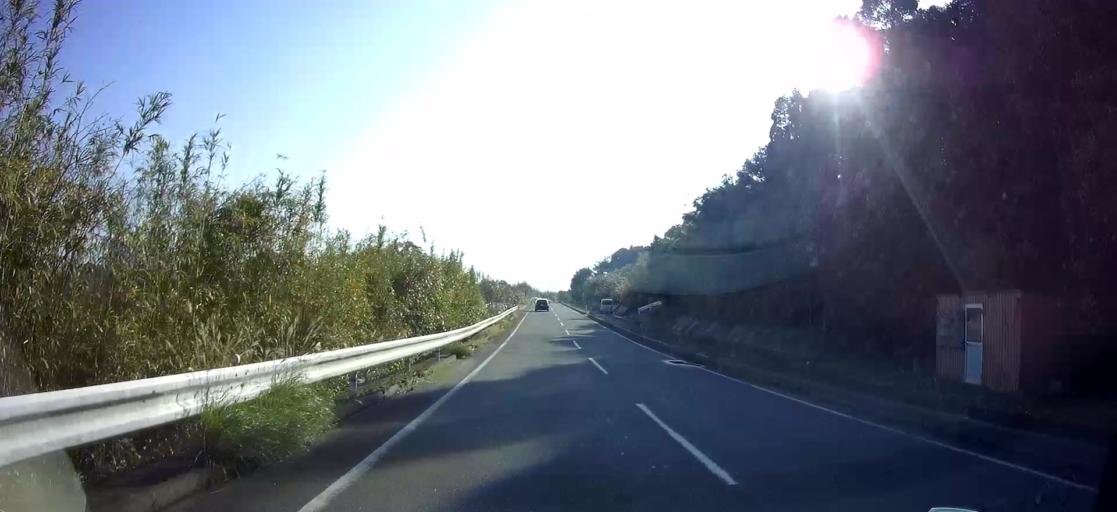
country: JP
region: Kumamoto
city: Minamata
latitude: 32.4011
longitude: 130.3995
